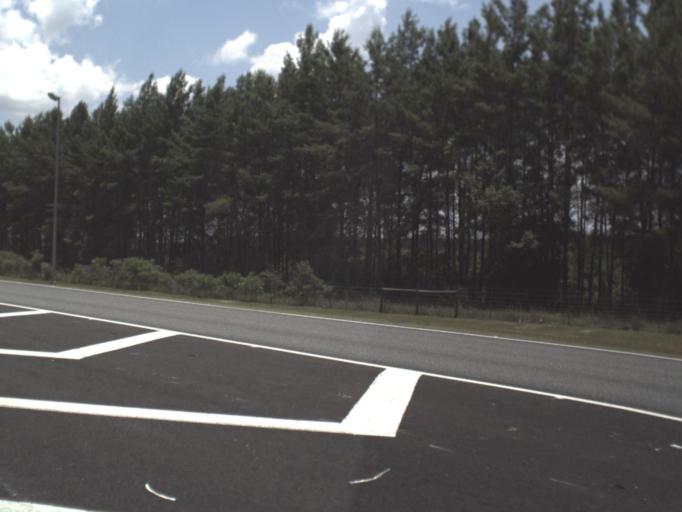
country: US
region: Florida
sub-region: Madison County
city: Madison
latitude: 30.3721
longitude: -83.2652
